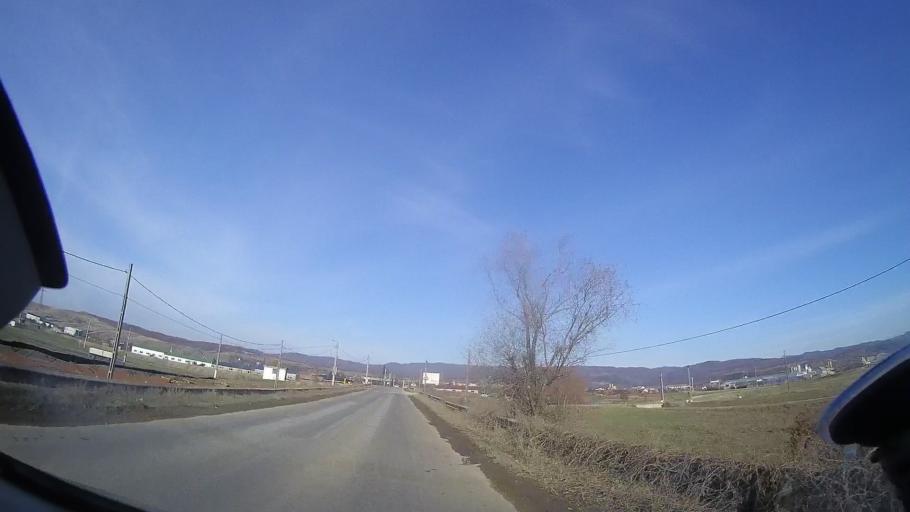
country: RO
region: Bihor
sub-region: Comuna Astileu
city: Astileu
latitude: 47.0467
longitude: 22.3911
